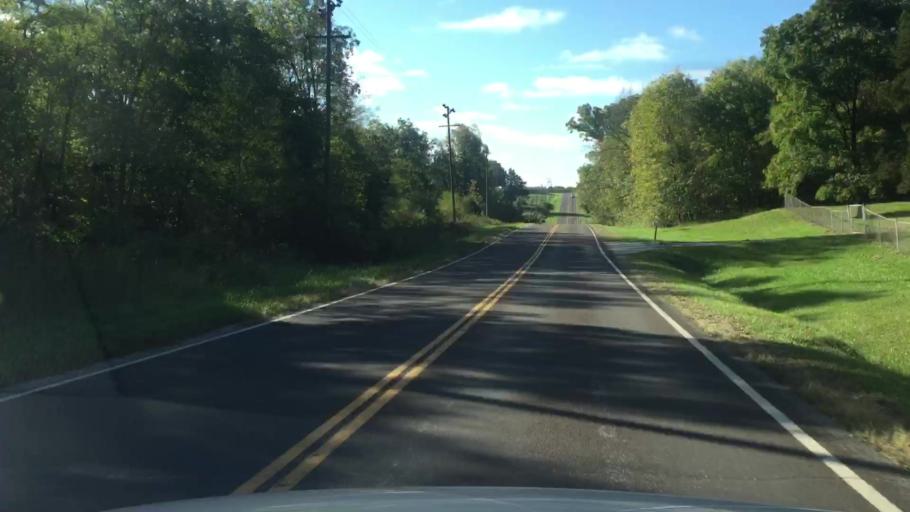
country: US
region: Missouri
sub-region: Howard County
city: New Franklin
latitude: 39.0511
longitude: -92.7444
